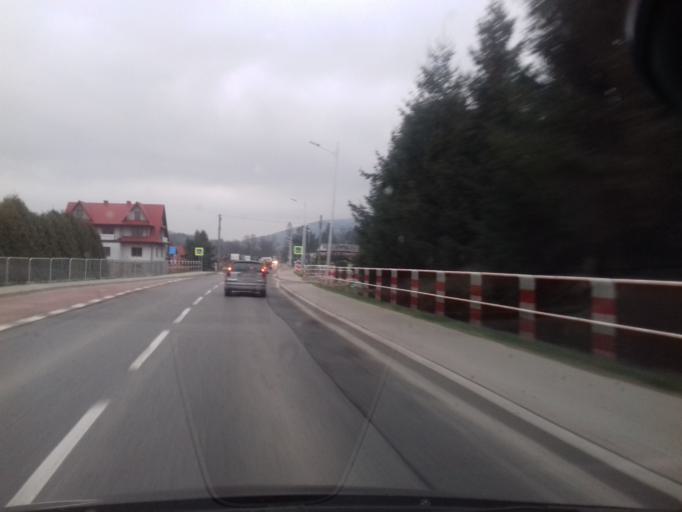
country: PL
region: Lesser Poland Voivodeship
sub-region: Powiat limanowski
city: Mszana Dolna
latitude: 49.6902
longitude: 20.0463
